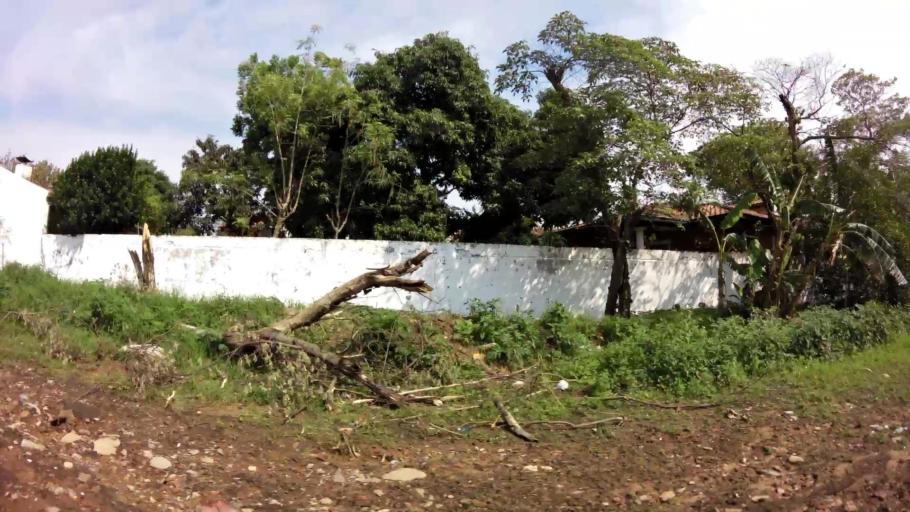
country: PY
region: Asuncion
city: Asuncion
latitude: -25.2647
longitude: -57.5618
